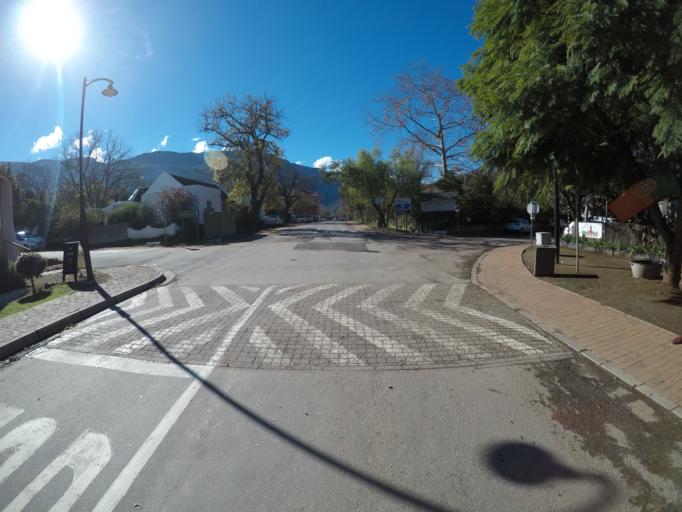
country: ZA
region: Western Cape
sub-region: Overberg District Municipality
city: Caledon
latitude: -34.0513
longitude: 19.6066
